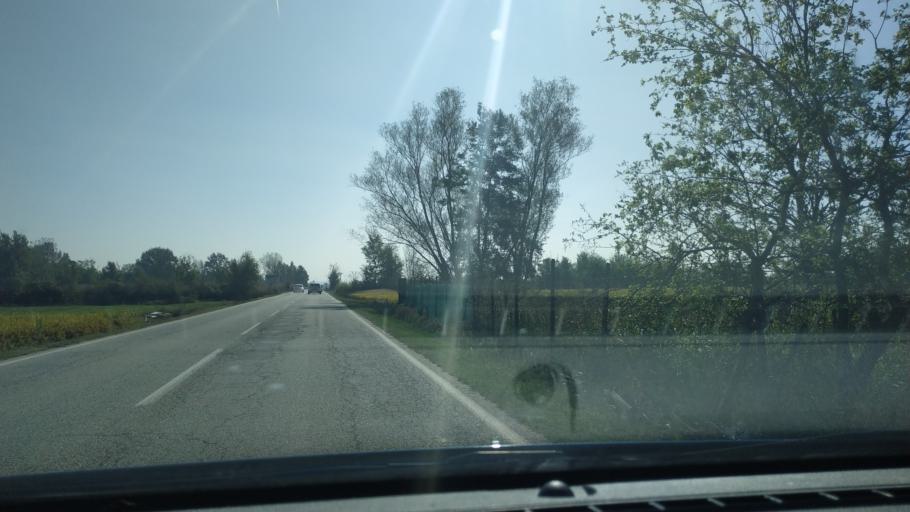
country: IT
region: Piedmont
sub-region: Provincia di Alessandria
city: Borgo San Martino
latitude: 45.1090
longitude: 8.5125
